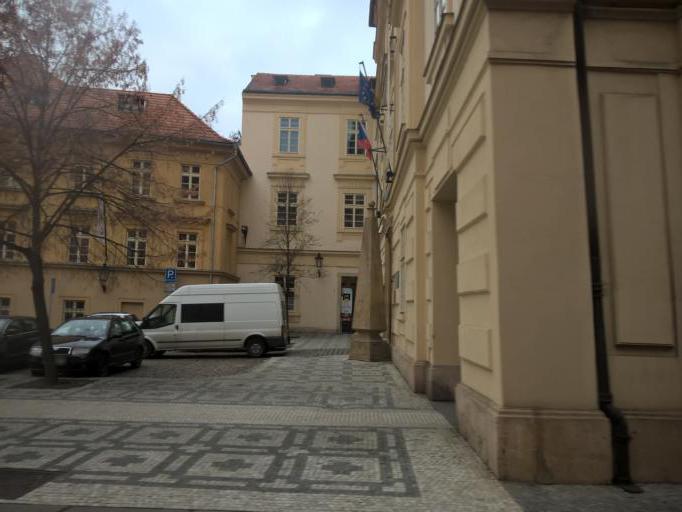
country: CZ
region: Praha
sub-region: Praha 1
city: Mala Strana
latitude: 50.0850
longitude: 14.4043
